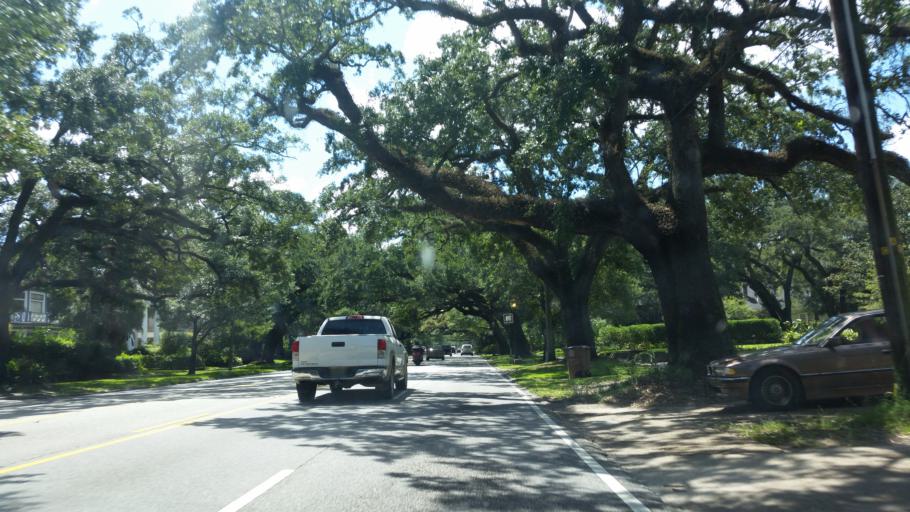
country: US
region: Alabama
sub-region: Mobile County
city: Mobile
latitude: 30.6836
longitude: -88.0626
